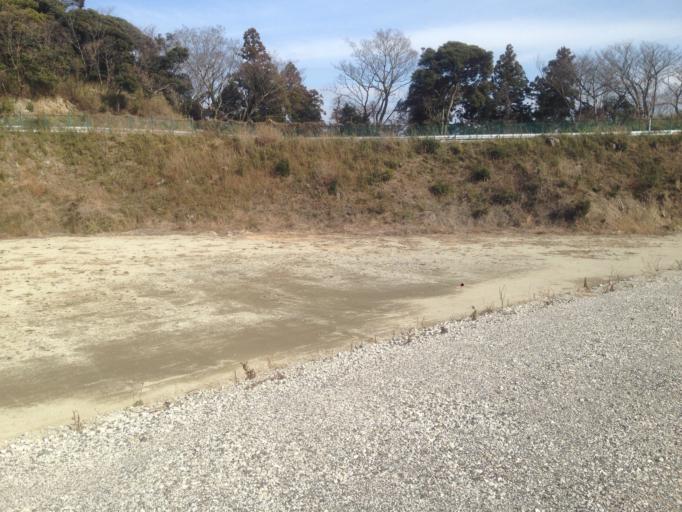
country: JP
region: Kanagawa
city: Yokosuka
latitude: 35.2462
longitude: 139.6441
